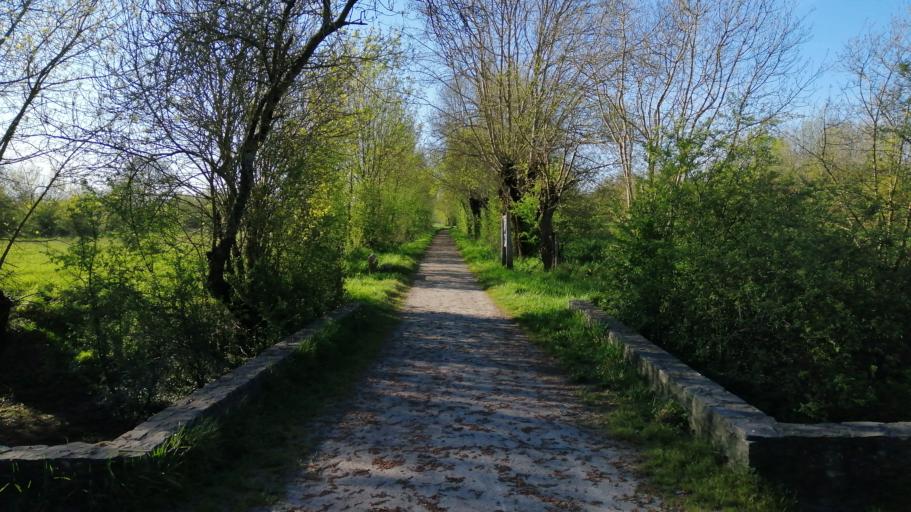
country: FR
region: Pays de la Loire
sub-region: Departement de la Loire-Atlantique
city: Saint-Gereon
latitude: 47.3616
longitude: -1.1959
